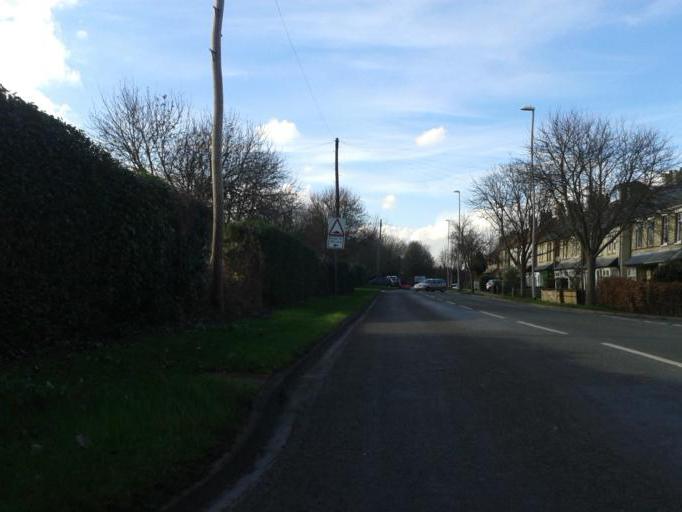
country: GB
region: England
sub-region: Cambridgeshire
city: Fulbourn
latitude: 52.1833
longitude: 0.1757
